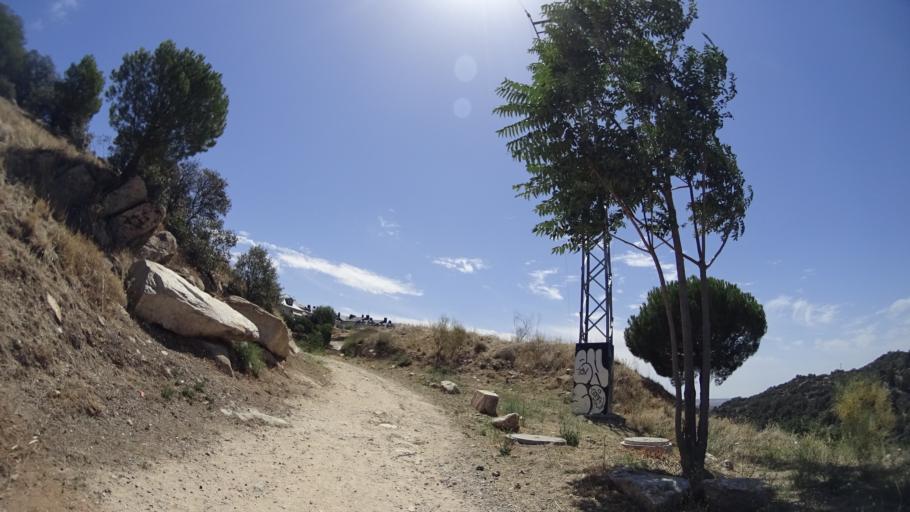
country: ES
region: Madrid
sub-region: Provincia de Madrid
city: Torrelodones
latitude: 40.5708
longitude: -3.9296
